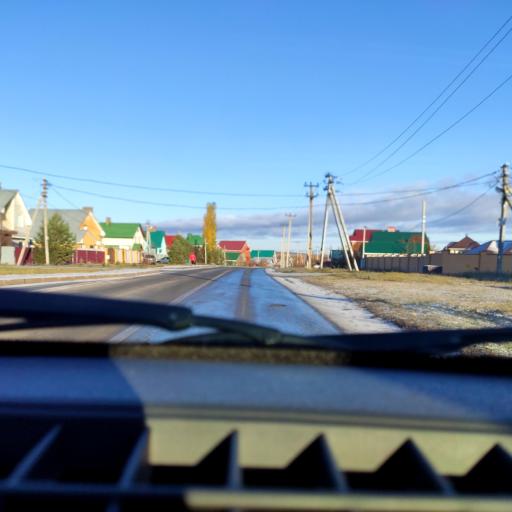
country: RU
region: Bashkortostan
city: Avdon
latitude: 54.6942
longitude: 55.7975
